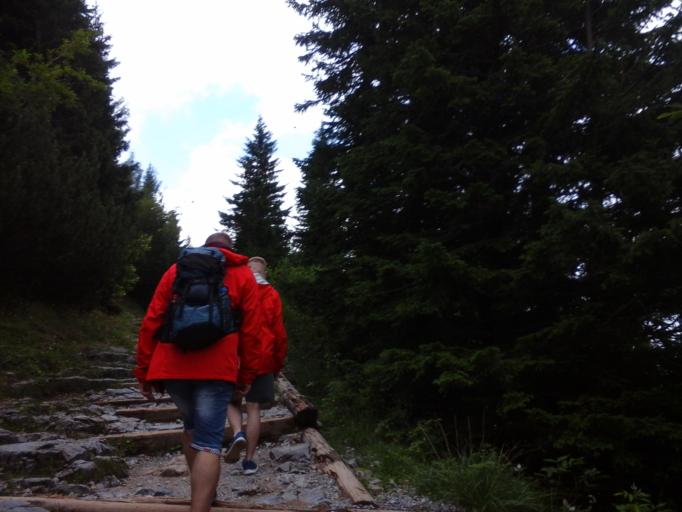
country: PL
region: Lesser Poland Voivodeship
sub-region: Powiat tatrzanski
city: Zakopane
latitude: 49.2473
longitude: 20.0074
